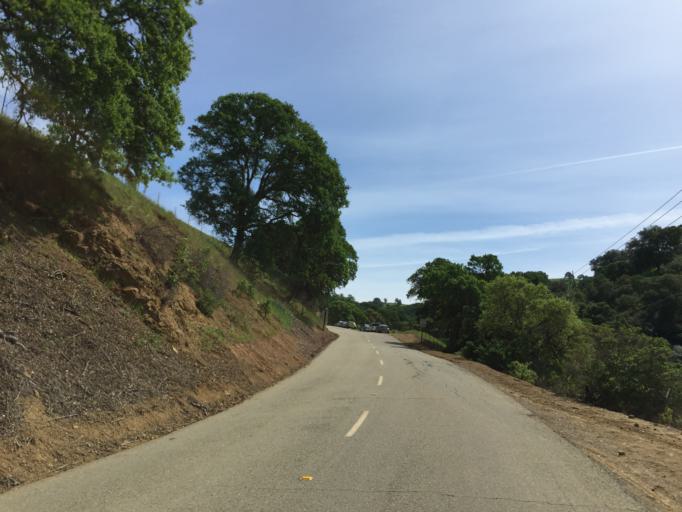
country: US
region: California
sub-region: Contra Costa County
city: Diablo
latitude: 37.8860
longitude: -121.9787
